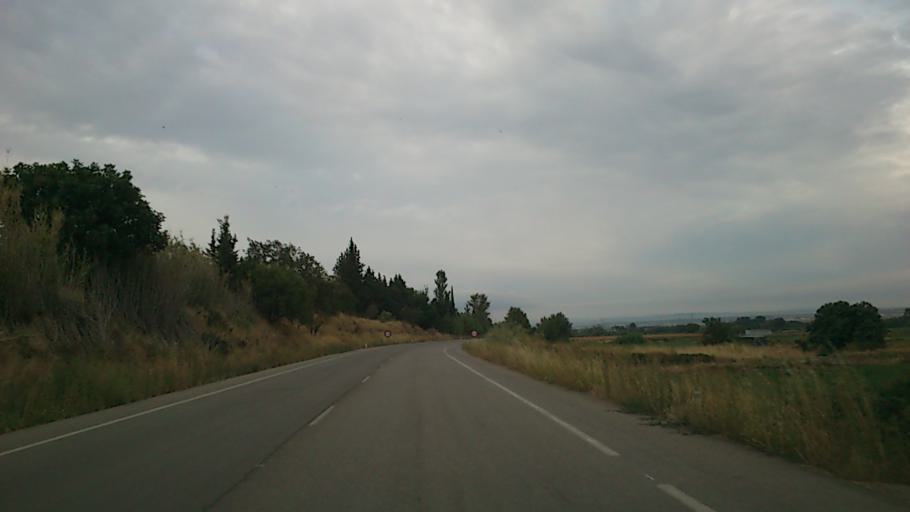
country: ES
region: Aragon
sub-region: Provincia de Zaragoza
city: Villanueva de Gallego
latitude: 41.7702
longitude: -0.7931
